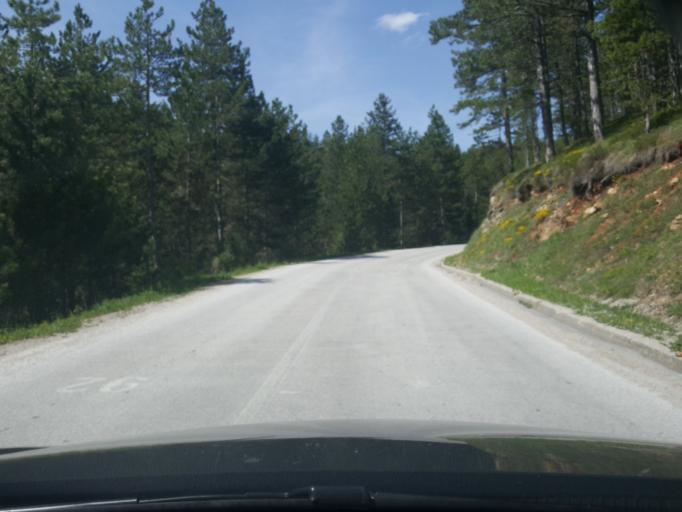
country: RS
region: Central Serbia
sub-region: Zlatiborski Okrug
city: Bajina Basta
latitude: 43.8771
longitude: 19.5658
